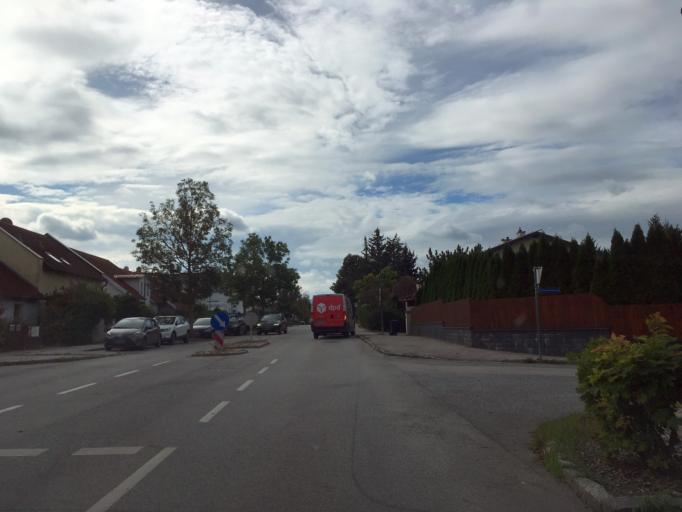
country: AT
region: Lower Austria
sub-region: Politischer Bezirk Modling
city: Gaaden
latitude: 48.0605
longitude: 16.2148
